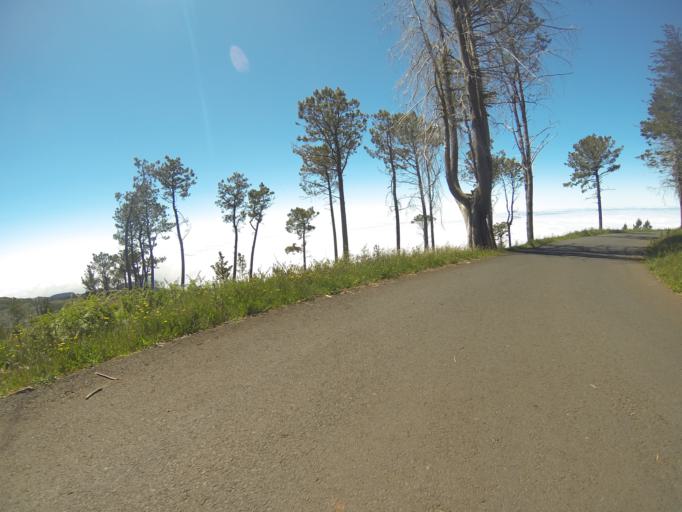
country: PT
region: Madeira
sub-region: Funchal
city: Nossa Senhora do Monte
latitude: 32.7082
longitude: -16.9099
